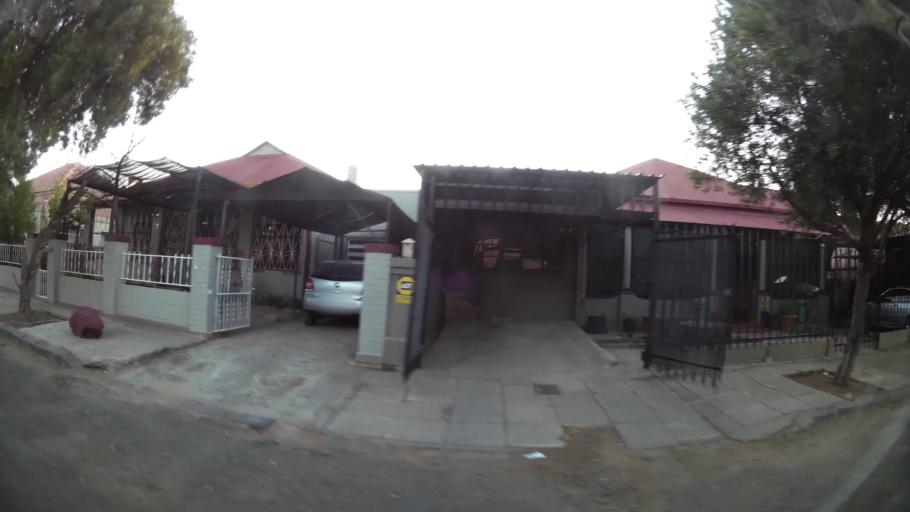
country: ZA
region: Northern Cape
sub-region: Frances Baard District Municipality
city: Kimberley
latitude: -28.7336
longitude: 24.7674
